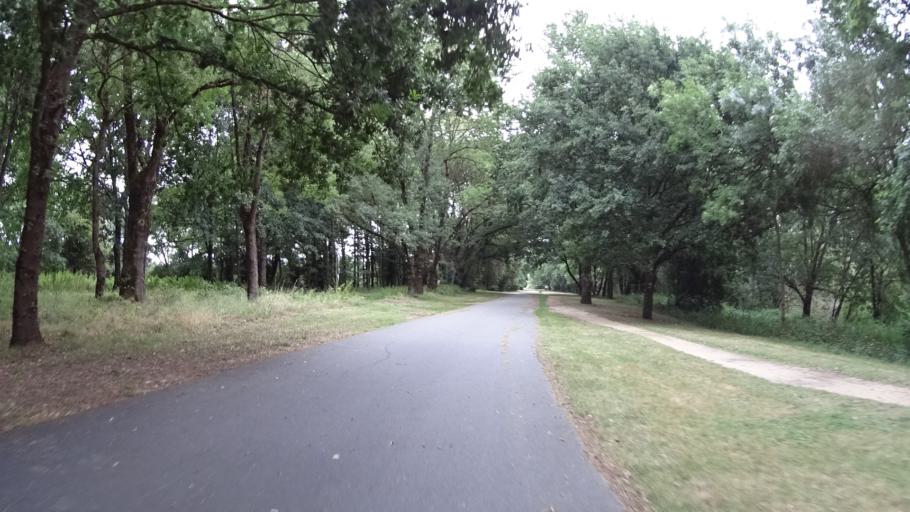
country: FR
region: Pays de la Loire
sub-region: Departement de la Loire-Atlantique
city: Sainte-Luce-sur-Loire
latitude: 47.2461
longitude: -1.4592
